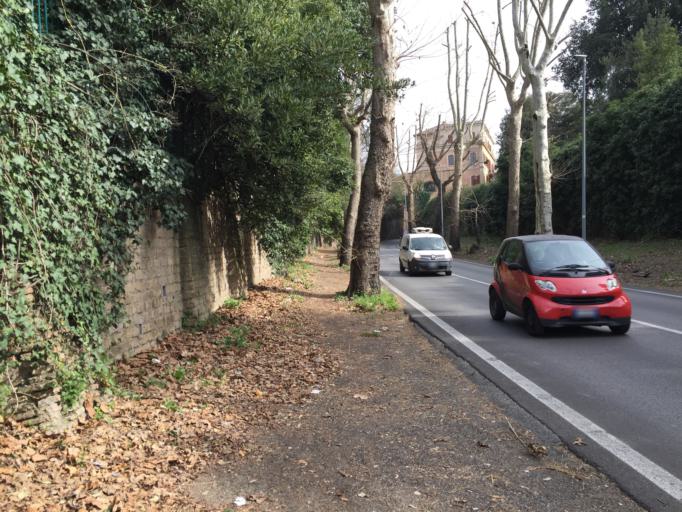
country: VA
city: Vatican City
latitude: 41.8889
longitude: 12.4538
